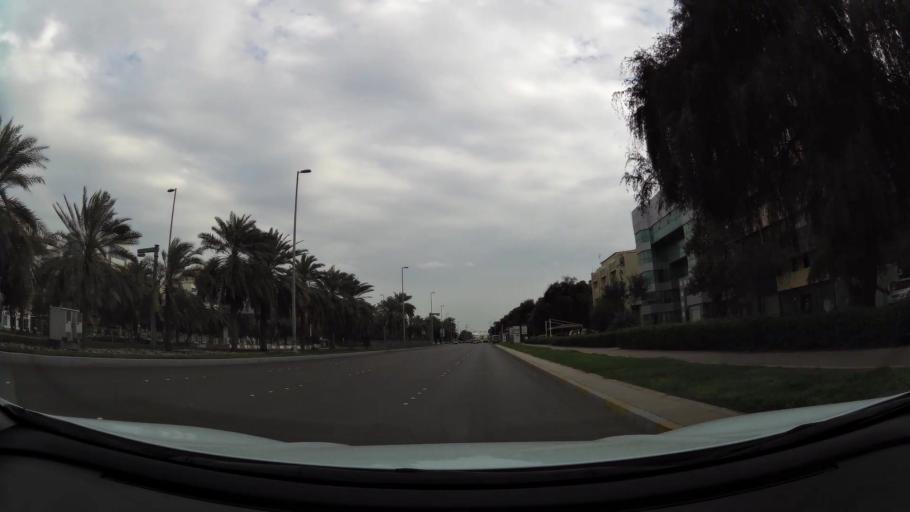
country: AE
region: Abu Dhabi
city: Abu Dhabi
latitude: 24.4478
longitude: 54.3998
